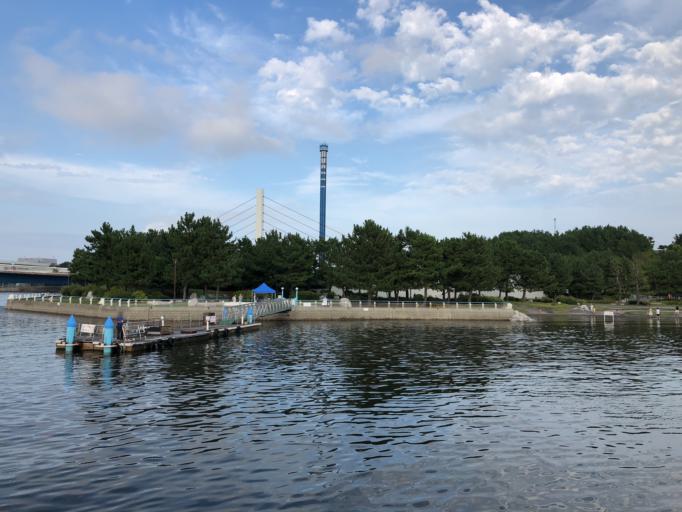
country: JP
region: Kanagawa
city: Yokosuka
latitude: 35.3375
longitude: 139.6414
